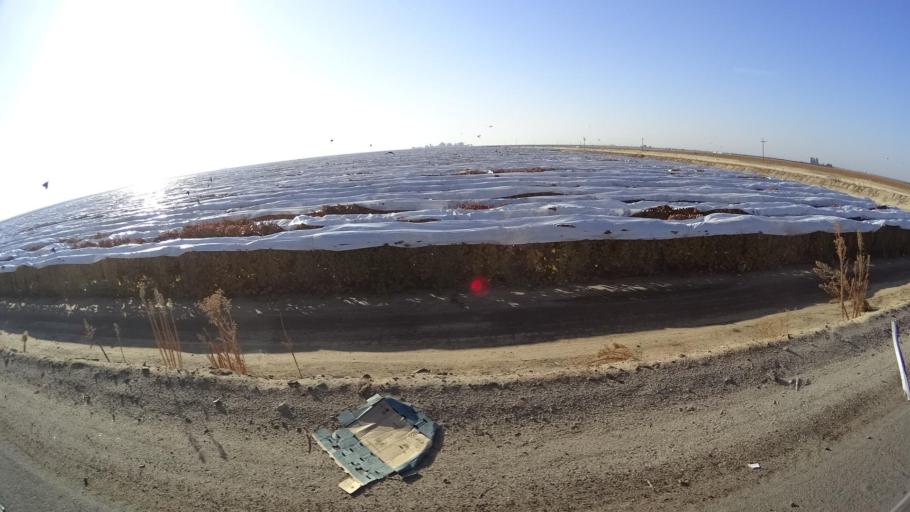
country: US
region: California
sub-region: Kern County
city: Delano
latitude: 35.7687
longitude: -119.1760
